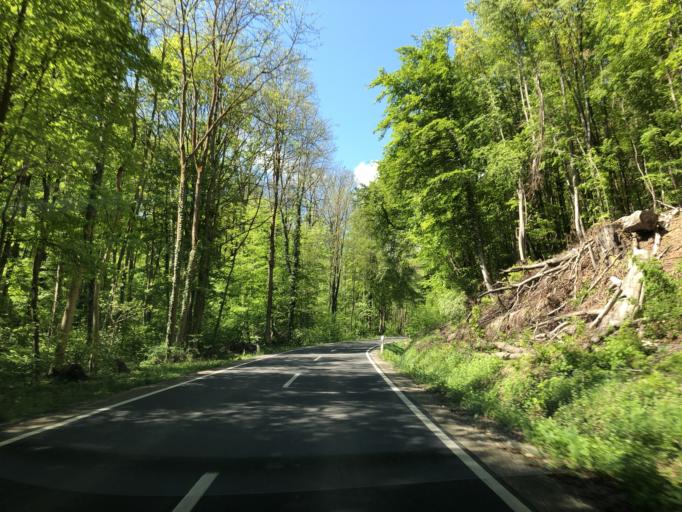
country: DE
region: Hesse
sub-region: Regierungsbezirk Kassel
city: Bad Sooden-Allendorf
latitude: 51.2676
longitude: 9.9436
